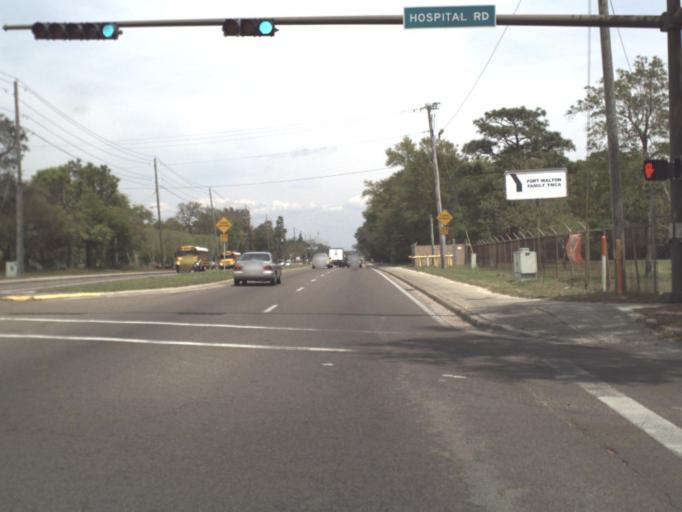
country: US
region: Florida
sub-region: Okaloosa County
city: Wright
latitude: 30.4586
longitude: -86.6341
